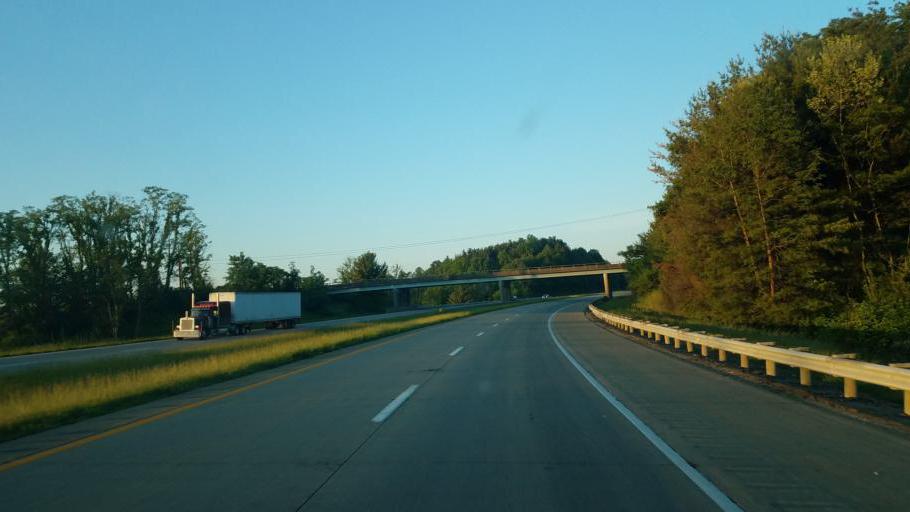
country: US
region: Ohio
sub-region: Washington County
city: Devola
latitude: 39.5294
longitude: -81.4444
